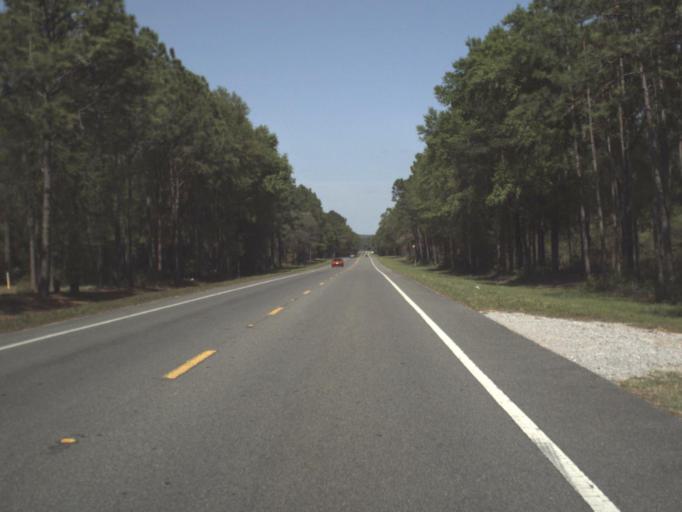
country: US
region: Florida
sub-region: Okaloosa County
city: Crestview
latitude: 30.7401
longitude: -86.6511
